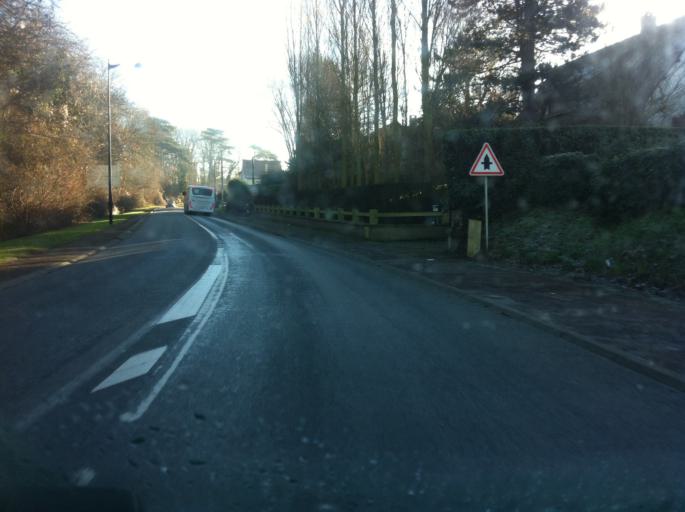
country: FR
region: Picardie
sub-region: Departement de la Somme
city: Mers-les-Bains
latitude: 50.0526
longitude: 1.3997
